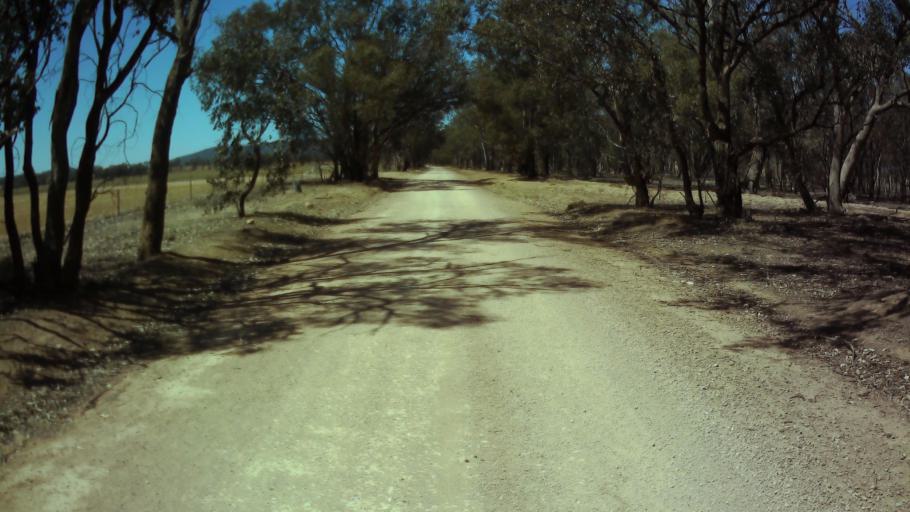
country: AU
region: New South Wales
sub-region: Weddin
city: Grenfell
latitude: -33.9213
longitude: 148.0787
